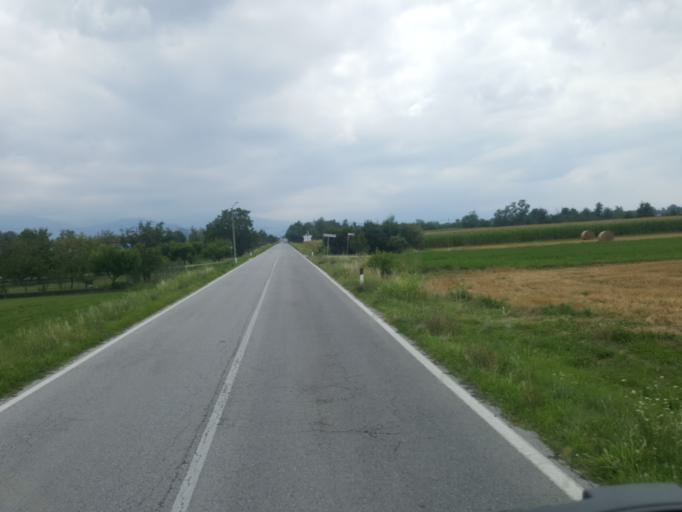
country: IT
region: Piedmont
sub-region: Provincia di Cuneo
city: Bastia Mondovi
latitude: 44.4366
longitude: 7.8670
